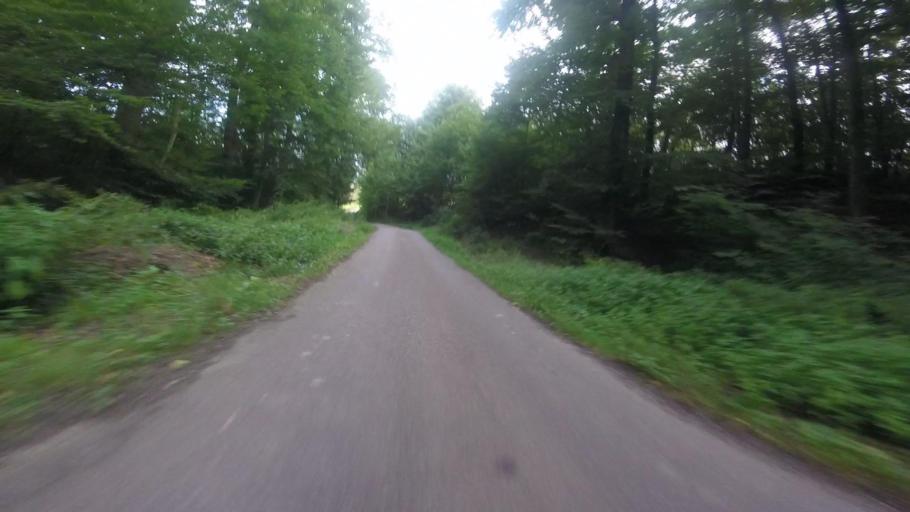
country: DE
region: Baden-Wuerttemberg
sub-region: Regierungsbezirk Stuttgart
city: Oberstenfeld
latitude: 49.0032
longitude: 9.3575
